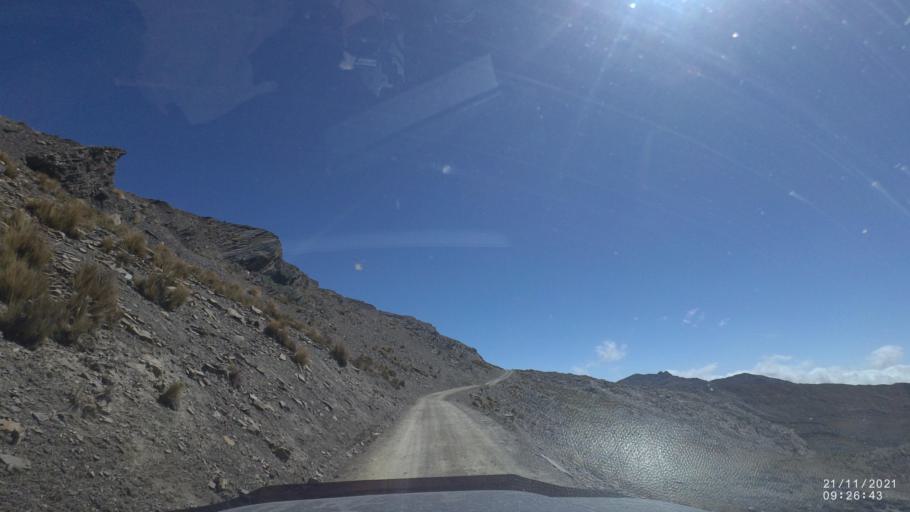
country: BO
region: Cochabamba
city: Cochabamba
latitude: -17.0861
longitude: -66.2535
